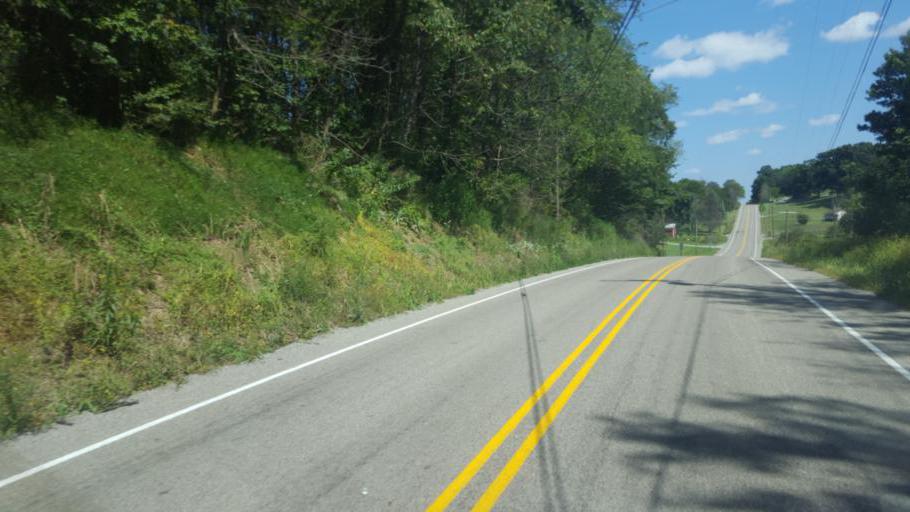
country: US
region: Pennsylvania
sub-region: Clarion County
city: Knox
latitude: 41.1095
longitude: -79.6148
